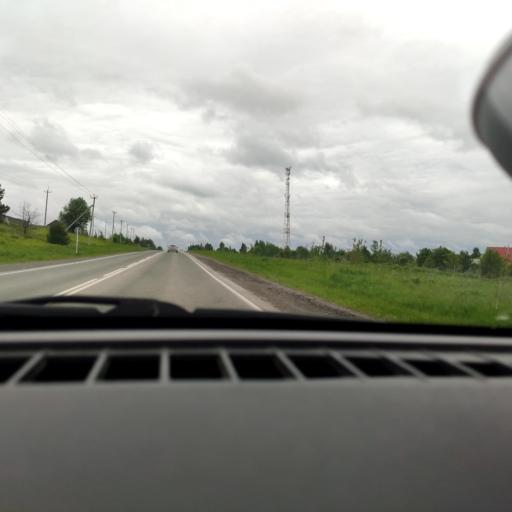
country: RU
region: Perm
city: Ust'-Kachka
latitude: 57.9450
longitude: 55.7394
